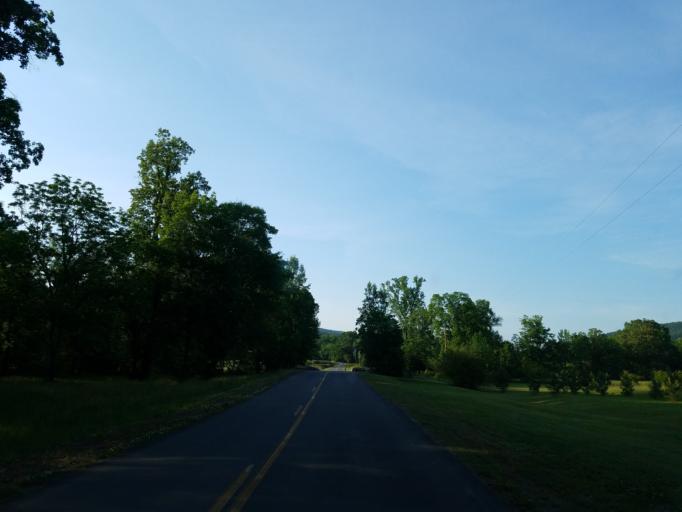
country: US
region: Georgia
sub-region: Gordon County
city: Calhoun
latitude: 34.5433
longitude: -85.1078
